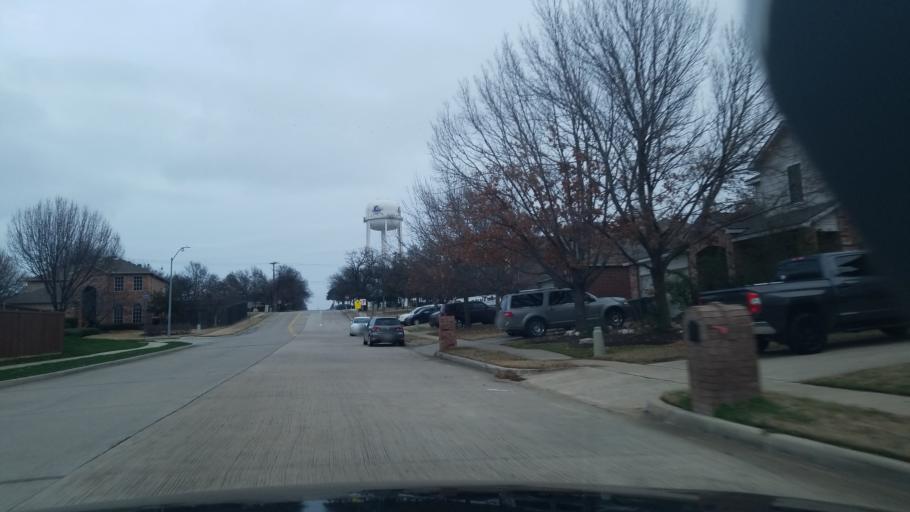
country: US
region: Texas
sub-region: Denton County
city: Corinth
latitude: 33.1360
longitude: -97.0661
